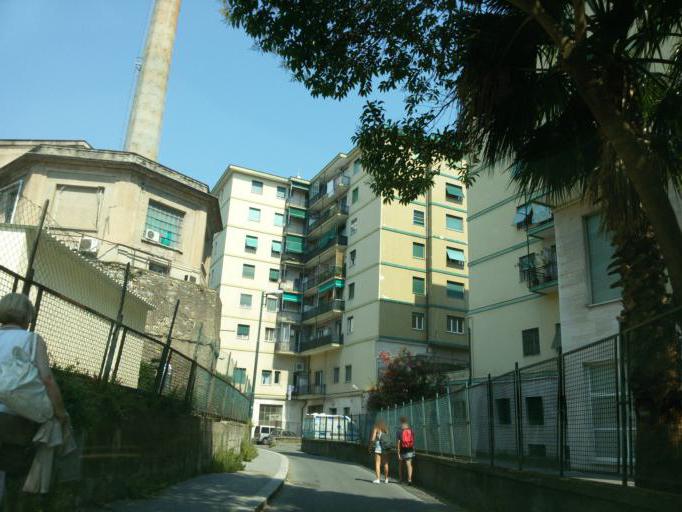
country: IT
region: Liguria
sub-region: Provincia di Genova
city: Genoa
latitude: 44.4070
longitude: 8.9709
